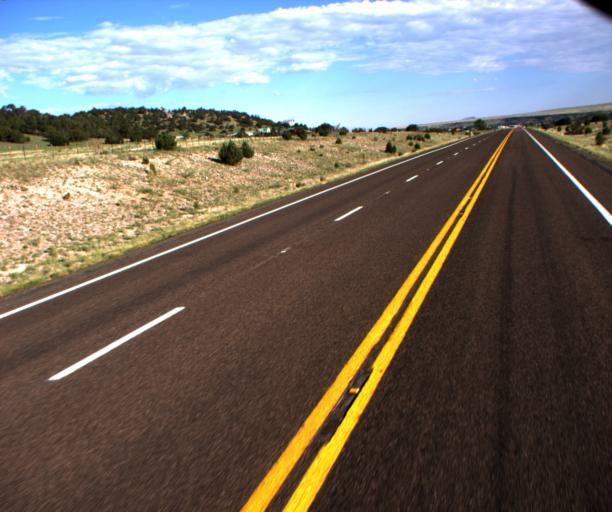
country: US
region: Arizona
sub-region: Apache County
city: Eagar
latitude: 34.0941
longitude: -109.2436
